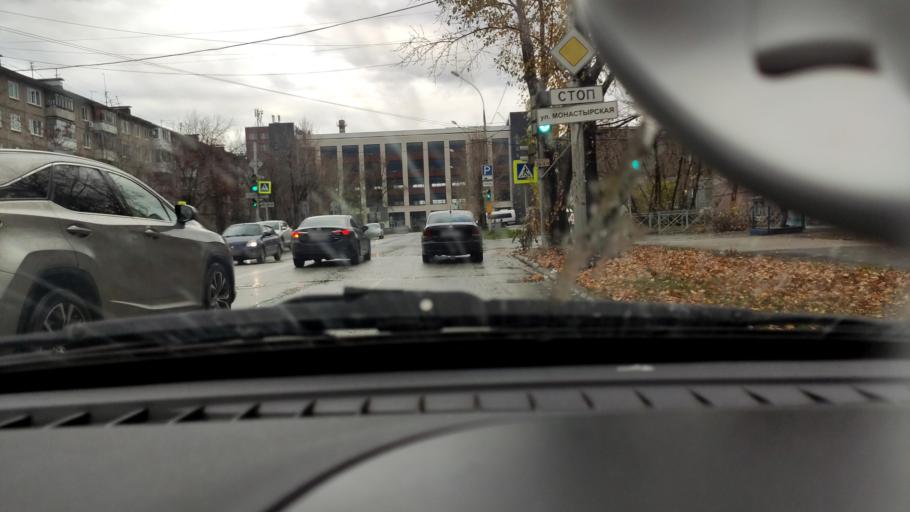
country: RU
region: Perm
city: Perm
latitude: 58.0110
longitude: 56.2103
